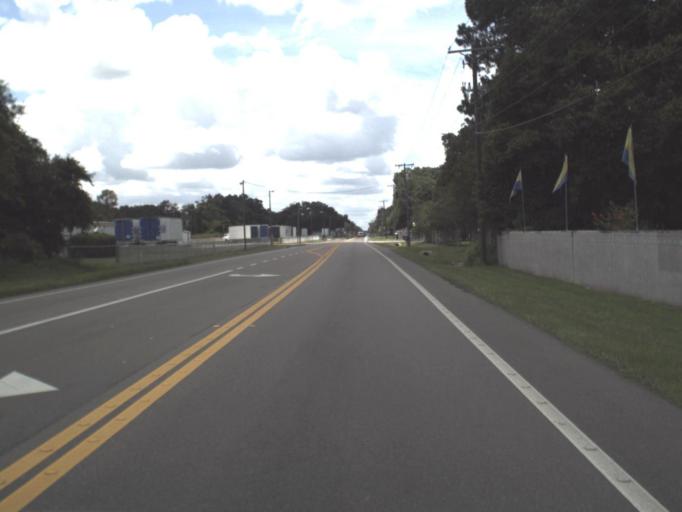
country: US
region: Florida
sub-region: Polk County
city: Winston
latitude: 28.0259
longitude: -82.0635
